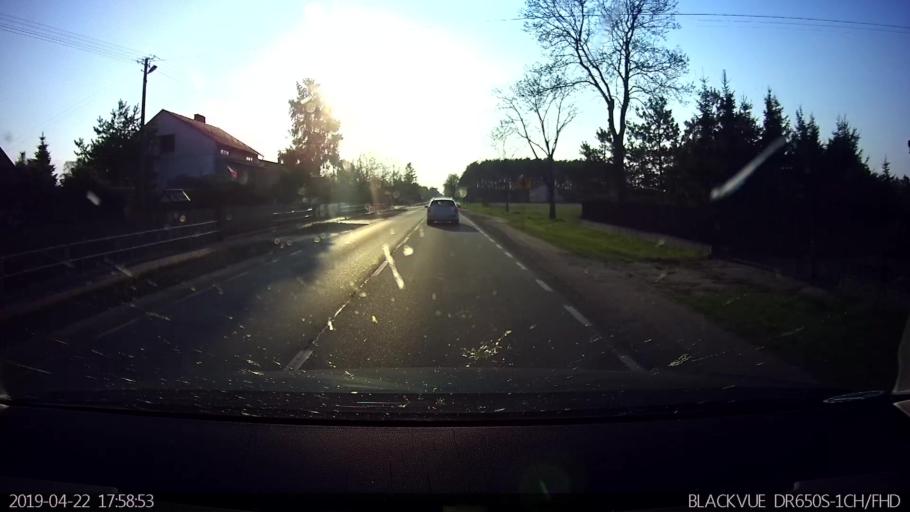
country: PL
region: Masovian Voivodeship
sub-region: Powiat wegrowski
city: Korytnica
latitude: 52.4729
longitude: 21.8695
